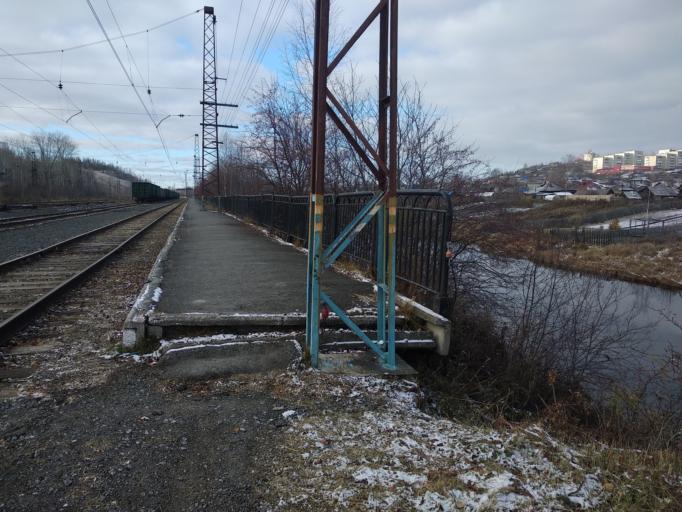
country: RU
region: Sverdlovsk
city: Karpinsk
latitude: 59.7537
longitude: 60.0258
